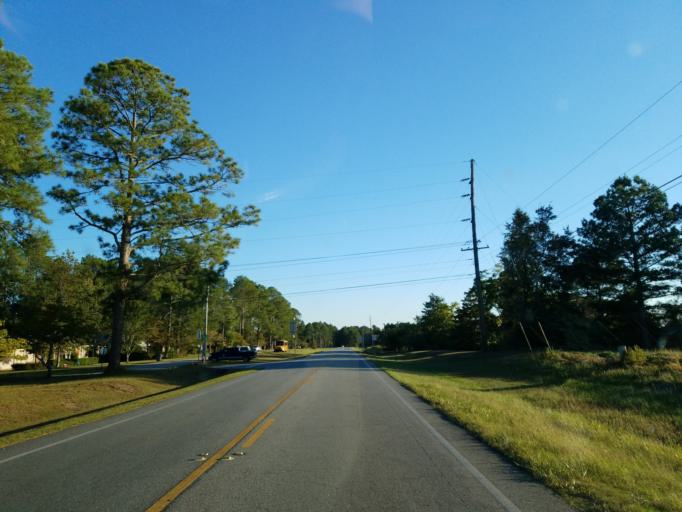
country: US
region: Georgia
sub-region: Worth County
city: Sylvester
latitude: 31.5451
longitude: -83.8431
